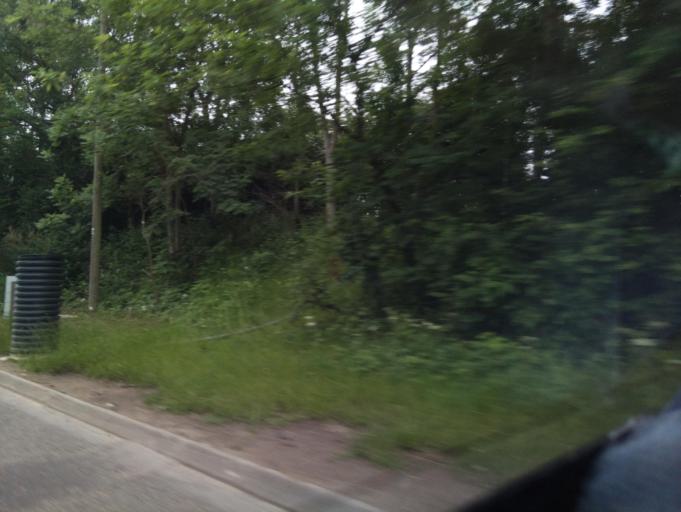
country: GB
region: England
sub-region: Leicestershire
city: Donisthorpe
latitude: 52.6904
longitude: -1.5503
